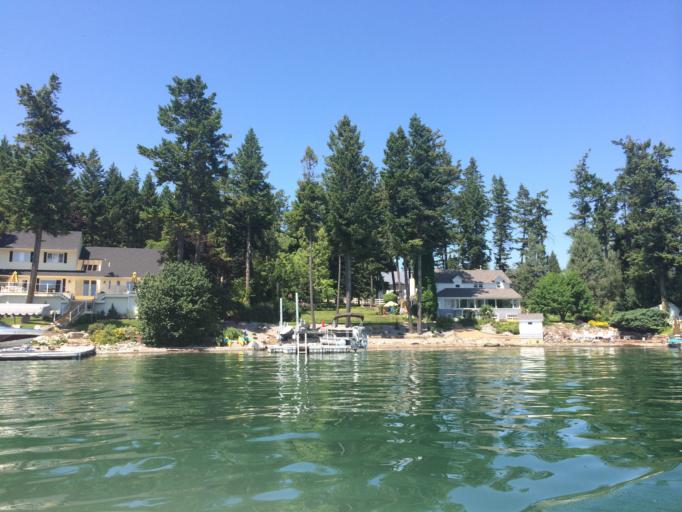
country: US
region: Montana
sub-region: Flathead County
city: Lakeside
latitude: 48.0362
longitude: -114.2200
